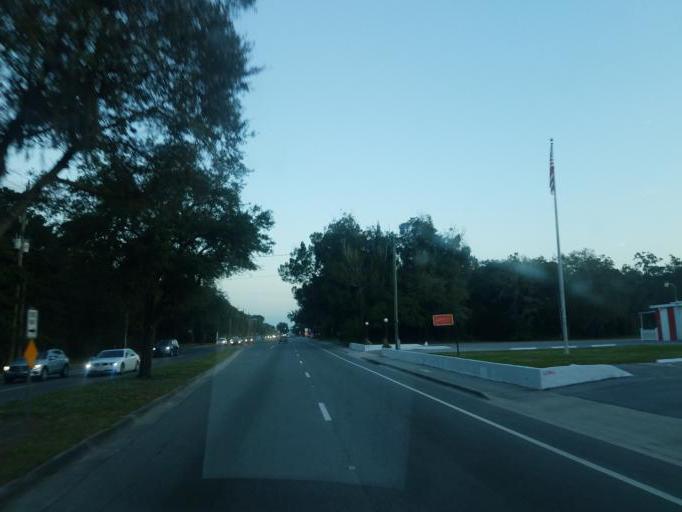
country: US
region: Florida
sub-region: Sarasota County
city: North Sarasota
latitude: 27.3787
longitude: -82.5056
